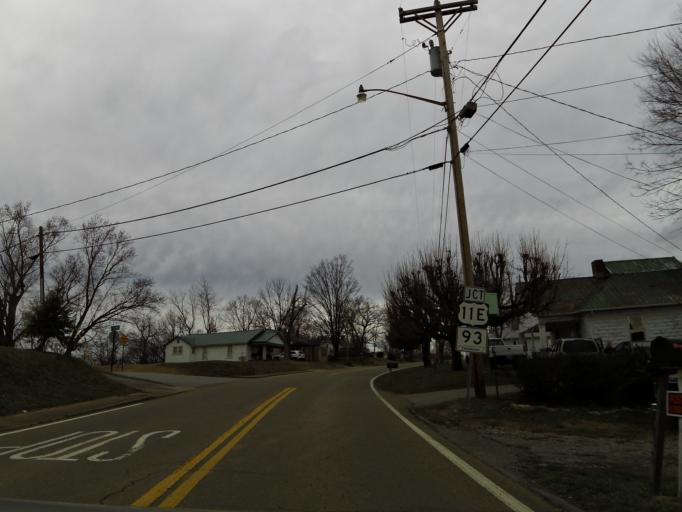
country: US
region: Tennessee
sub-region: Greene County
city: Greeneville
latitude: 36.1758
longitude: -82.8244
